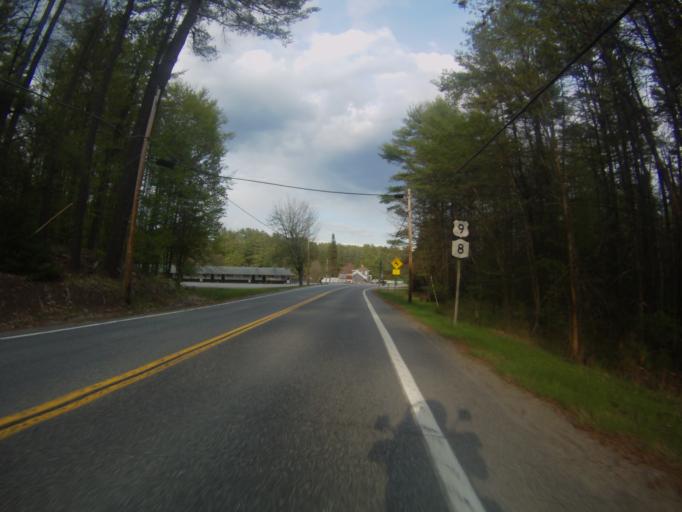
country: US
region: New York
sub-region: Warren County
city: Warrensburg
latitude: 43.6625
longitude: -73.8441
